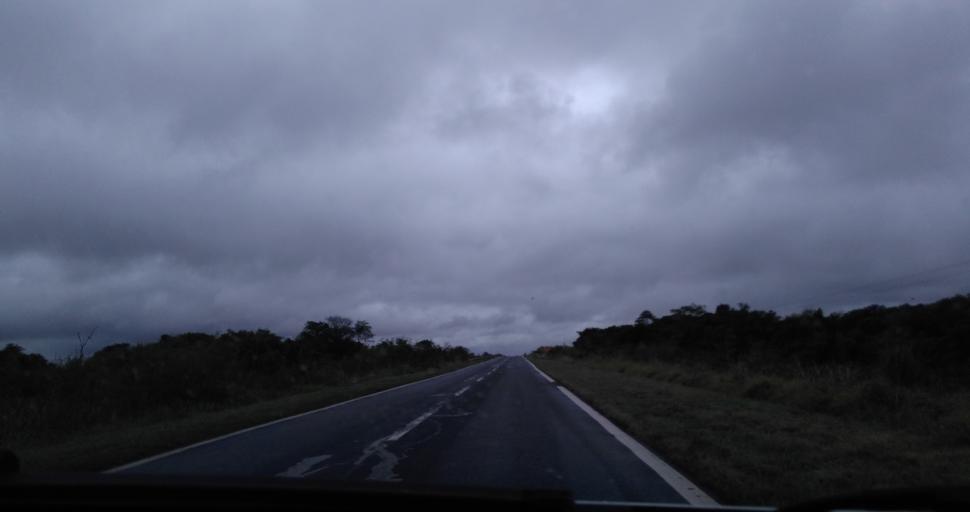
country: AR
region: Formosa
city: Clorinda
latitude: -25.6098
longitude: -57.9086
